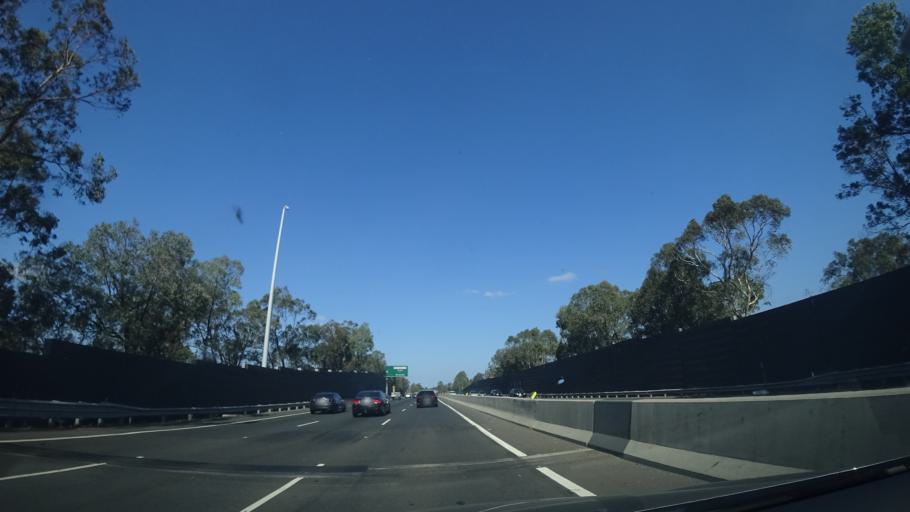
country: AU
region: New South Wales
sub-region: Bankstown
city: Revesby
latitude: -33.9397
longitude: 151.0110
